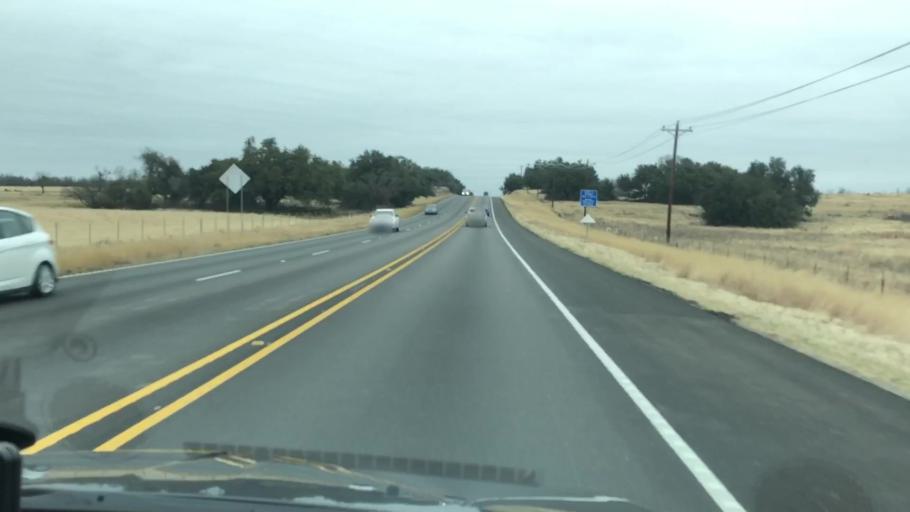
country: US
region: Texas
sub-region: Erath County
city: Stephenville
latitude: 32.3025
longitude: -98.1871
